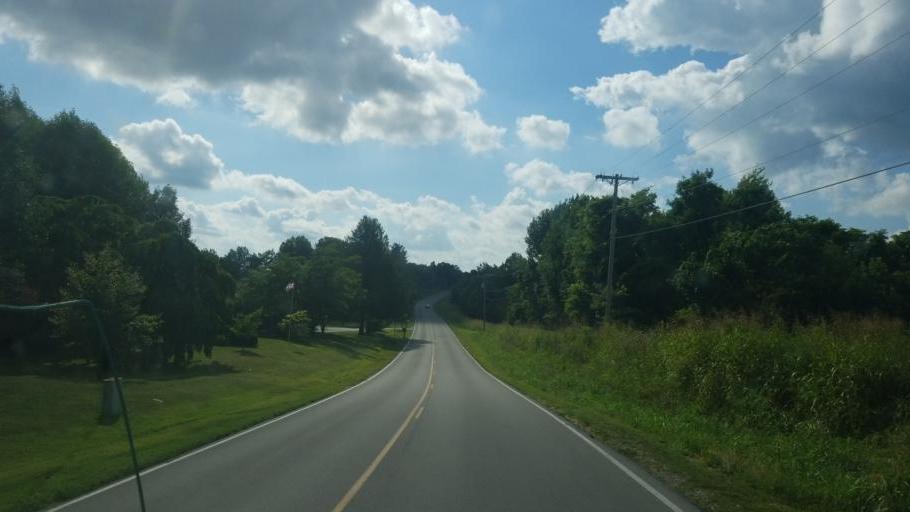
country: US
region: Illinois
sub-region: Union County
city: Cobden
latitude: 37.5563
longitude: -89.2980
